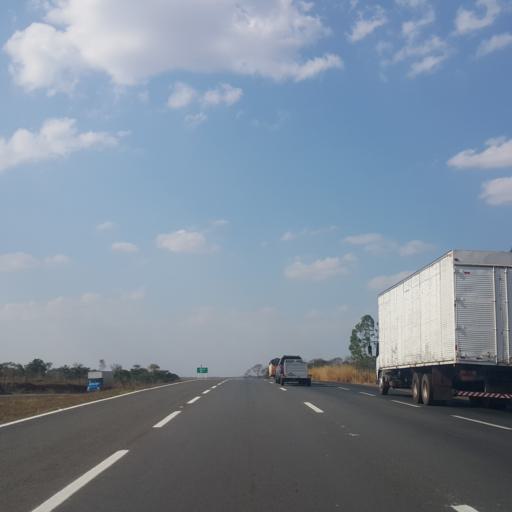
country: BR
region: Goias
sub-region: Abadiania
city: Abadiania
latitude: -16.2849
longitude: -48.7956
